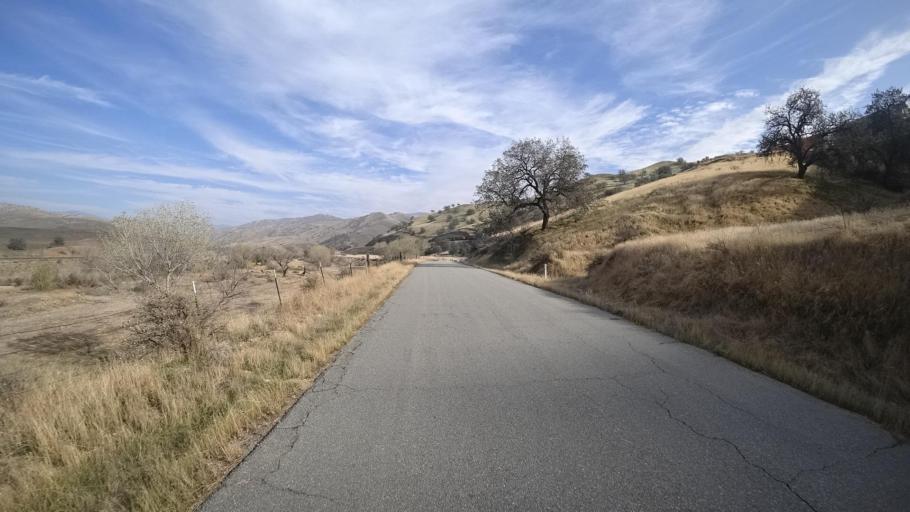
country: US
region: California
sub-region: Kern County
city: Bear Valley Springs
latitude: 35.2883
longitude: -118.6373
